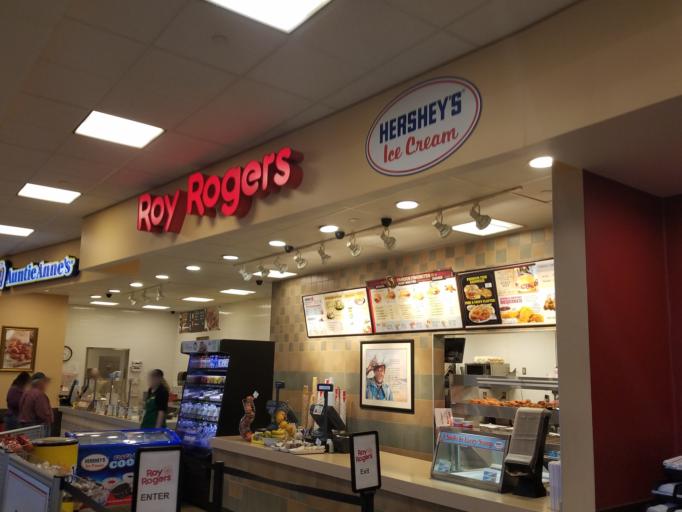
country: US
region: Pennsylvania
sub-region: Cumberland County
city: Carlisle
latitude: 40.2052
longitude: -77.2878
